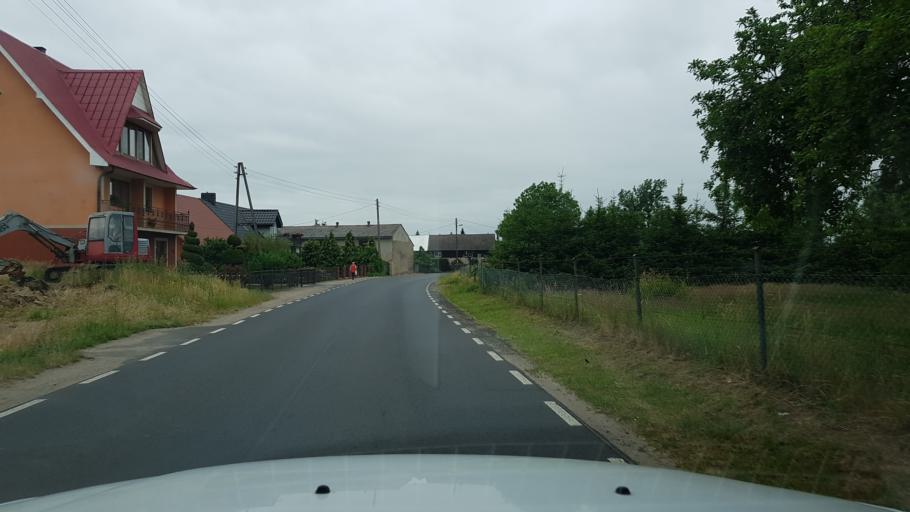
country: PL
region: West Pomeranian Voivodeship
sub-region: Powiat gryficki
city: Brojce
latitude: 53.9373
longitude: 15.4072
